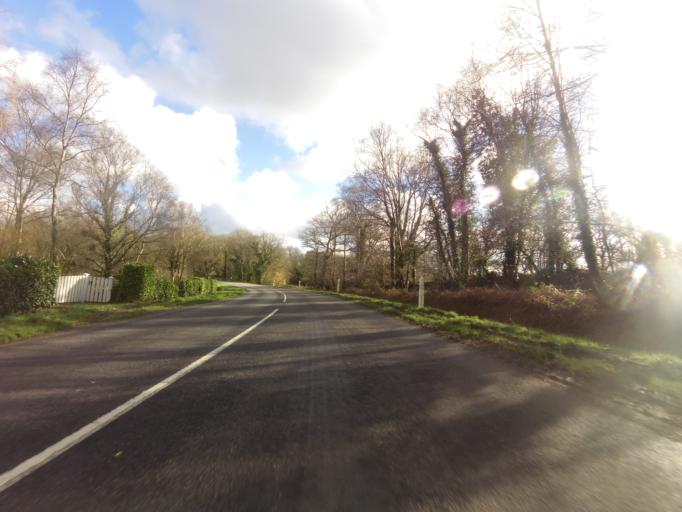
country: FR
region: Brittany
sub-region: Departement du Morbihan
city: Langonnet
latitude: 48.1422
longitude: -3.5303
